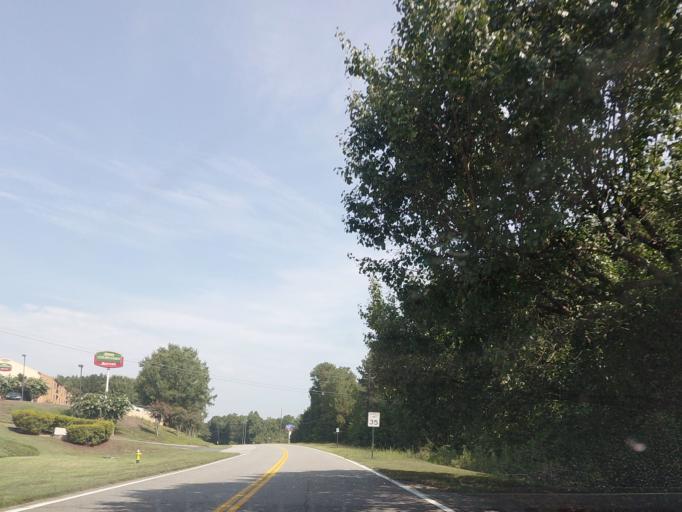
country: US
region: Georgia
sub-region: Bibb County
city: Macon
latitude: 32.9068
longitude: -83.6894
